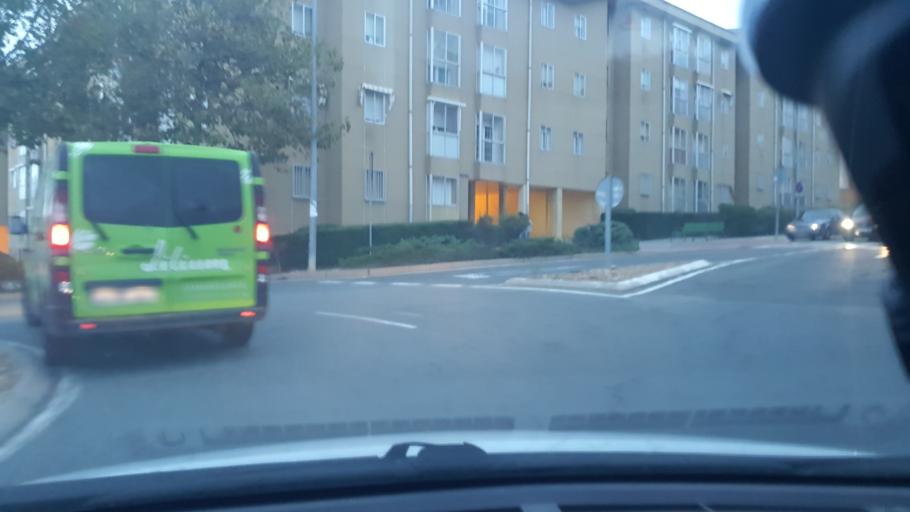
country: ES
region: Castille and Leon
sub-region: Provincia de Segovia
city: Segovia
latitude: 40.9328
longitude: -4.1029
